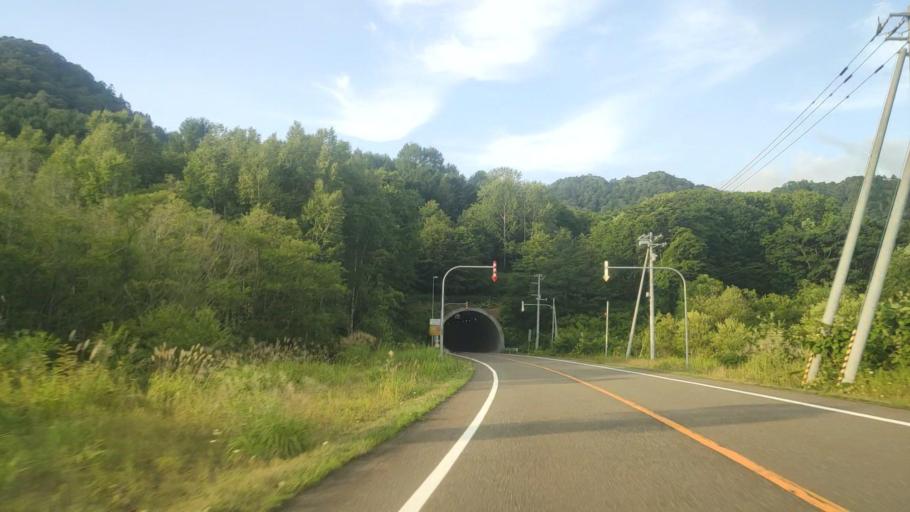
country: JP
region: Hokkaido
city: Iwamizawa
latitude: 43.0238
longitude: 142.0856
